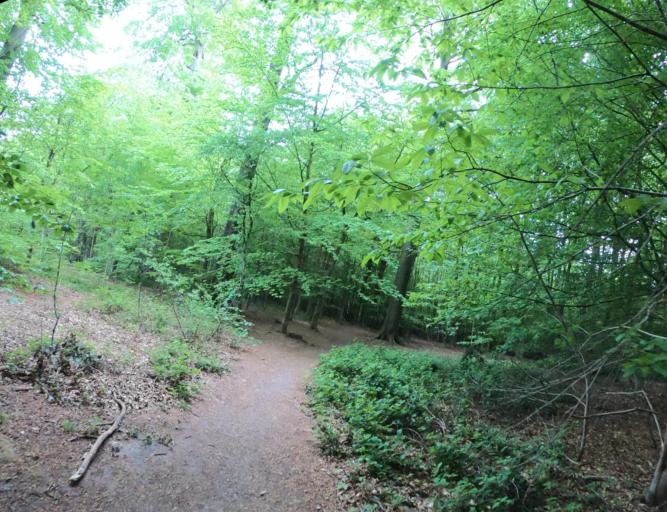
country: BE
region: Flanders
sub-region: Provincie Vlaams-Brabant
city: Beersel
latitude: 50.7418
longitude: 4.3078
